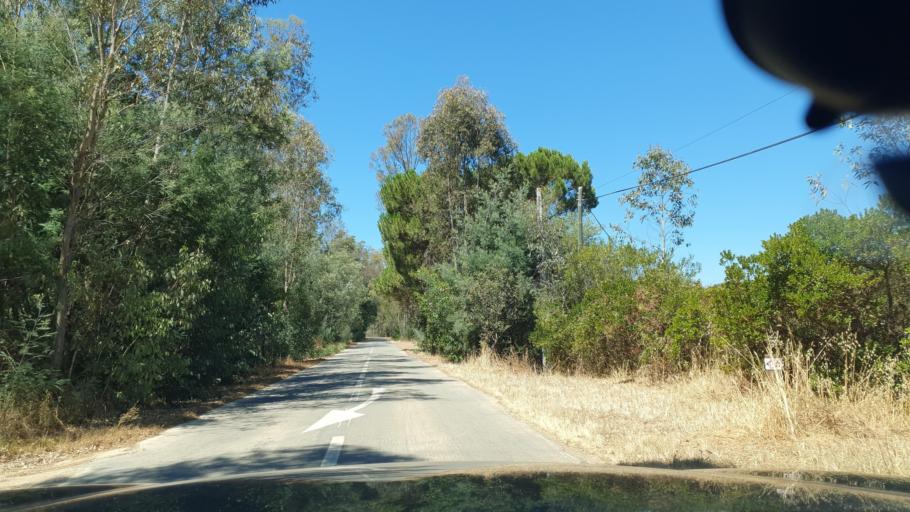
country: PT
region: Beja
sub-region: Odemira
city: Odemira
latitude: 37.5103
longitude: -8.4635
